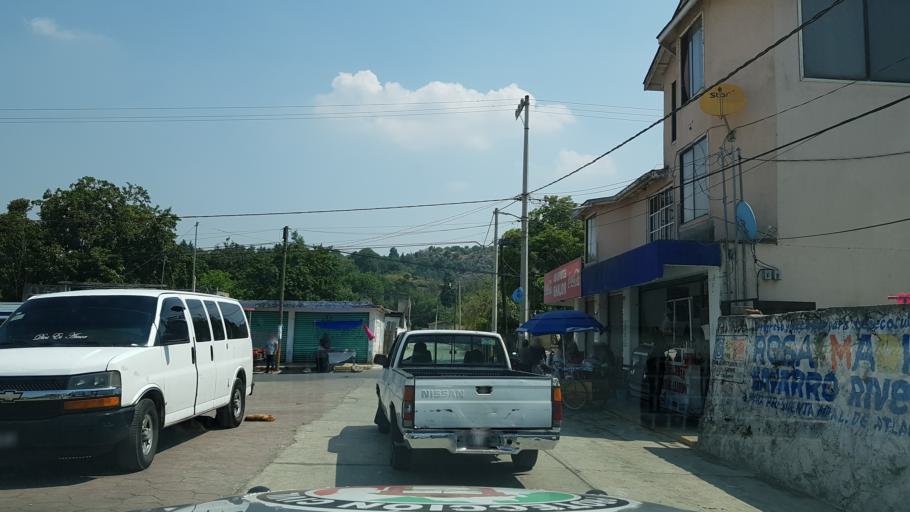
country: MX
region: Mexico
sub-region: Atlautla
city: San Juan Tepecoculco
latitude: 18.9847
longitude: -98.7876
